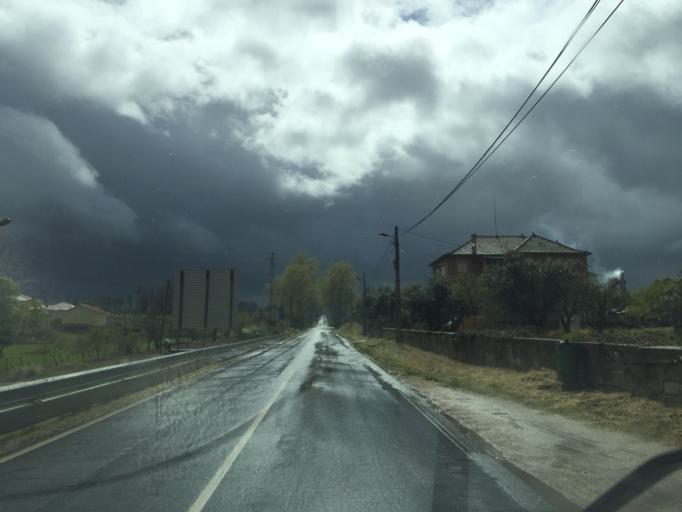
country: PT
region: Guarda
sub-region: Seia
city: Seia
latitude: 40.4220
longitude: -7.7342
